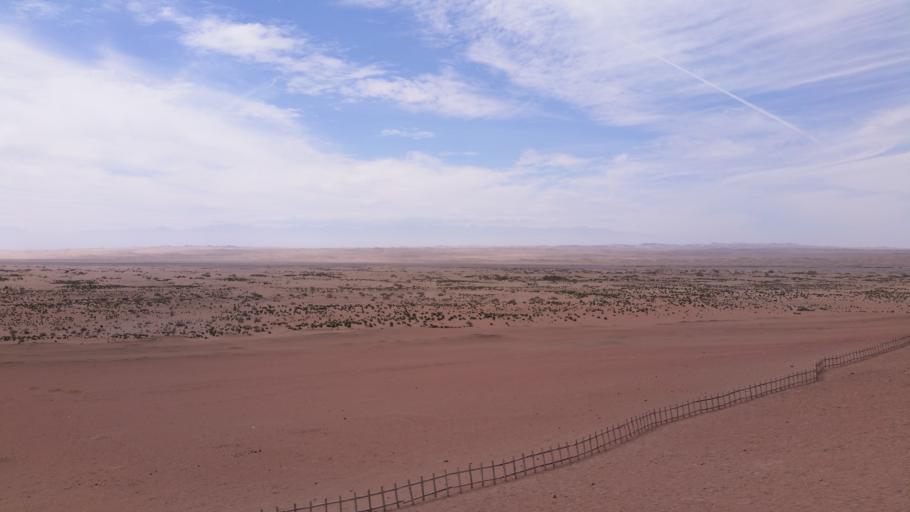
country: CN
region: Heilongjiang Sheng
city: Hongliuwan
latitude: 39.9257
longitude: 94.0586
